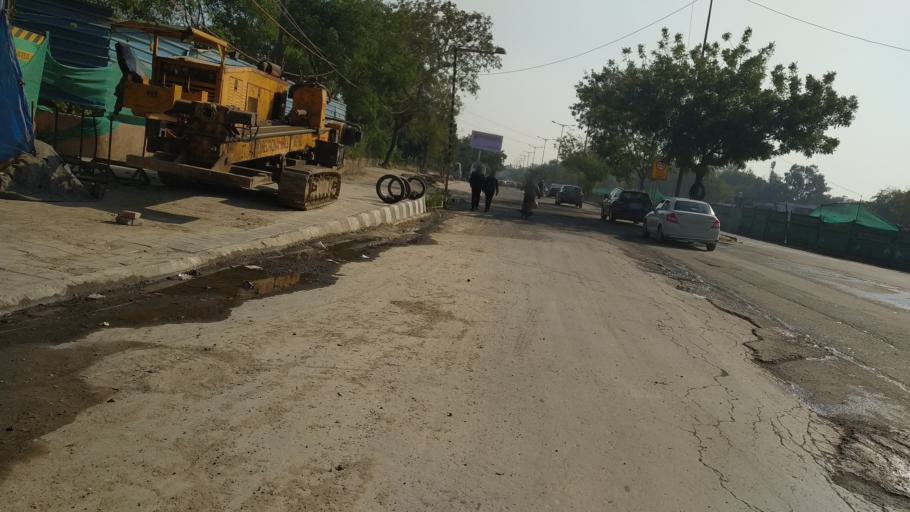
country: IN
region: NCT
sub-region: New Delhi
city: New Delhi
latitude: 28.6169
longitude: 77.2404
